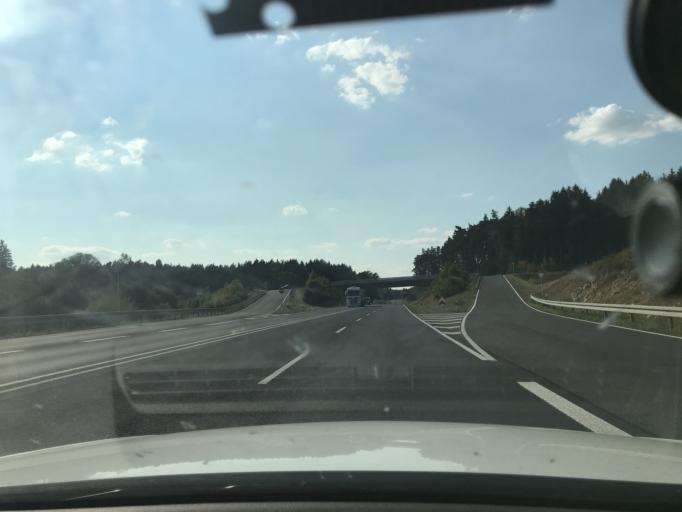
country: DE
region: Bavaria
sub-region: Upper Palatinate
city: Poppenricht
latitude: 49.4638
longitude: 11.7864
